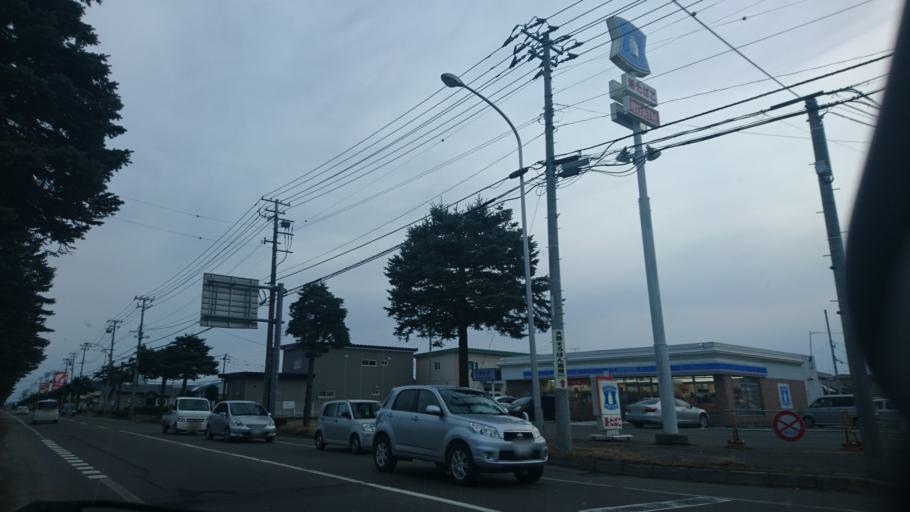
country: JP
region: Hokkaido
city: Otofuke
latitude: 42.9559
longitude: 143.1872
